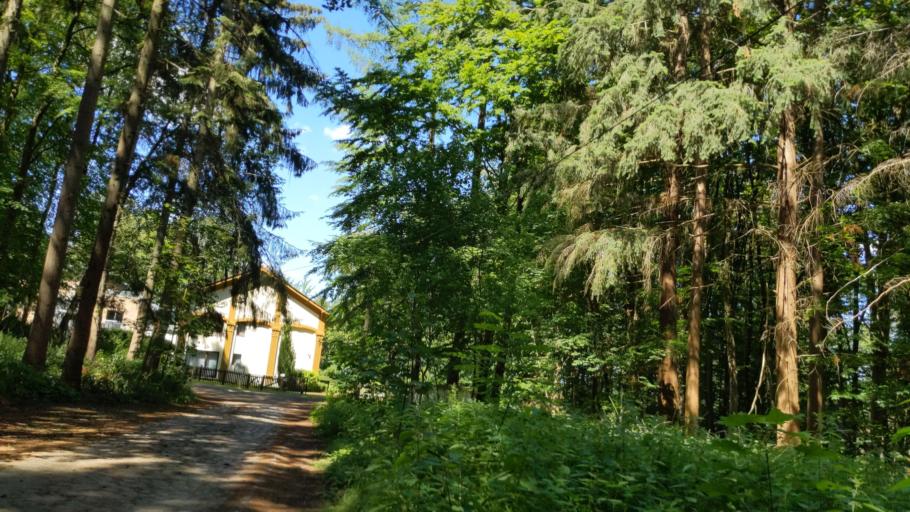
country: DE
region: Schleswig-Holstein
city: Schmilau
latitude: 53.6861
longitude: 10.7656
